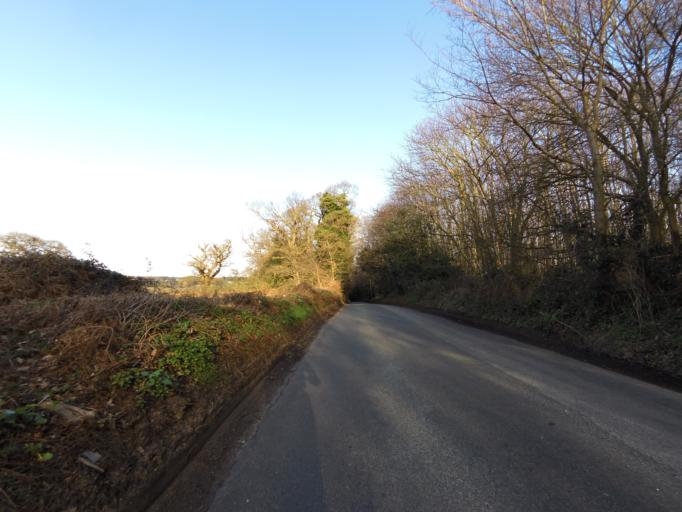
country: GB
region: England
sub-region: Suffolk
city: Kesgrave
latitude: 52.0791
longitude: 1.2727
